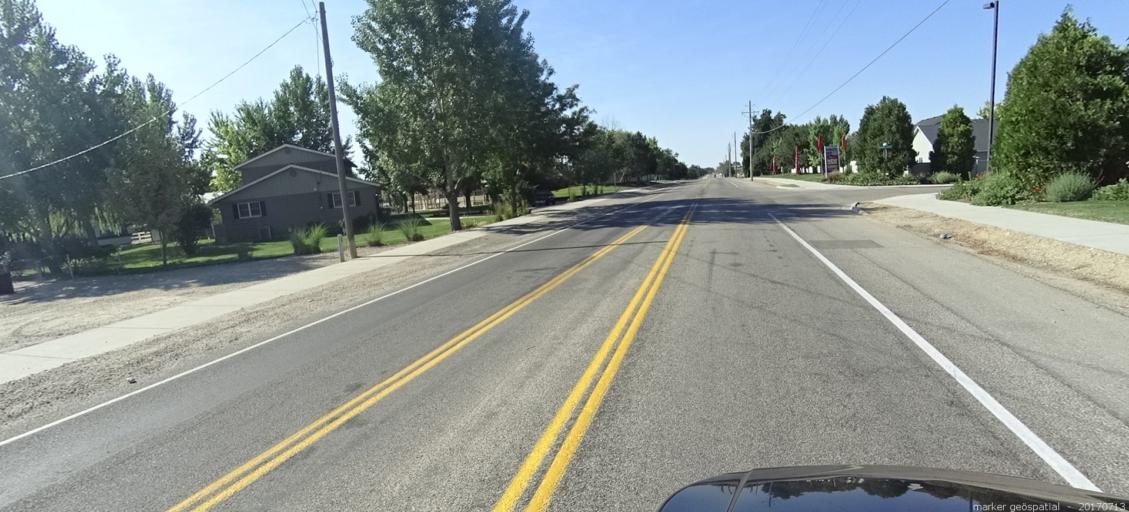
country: US
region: Idaho
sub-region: Ada County
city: Kuna
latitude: 43.5139
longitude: -116.4139
